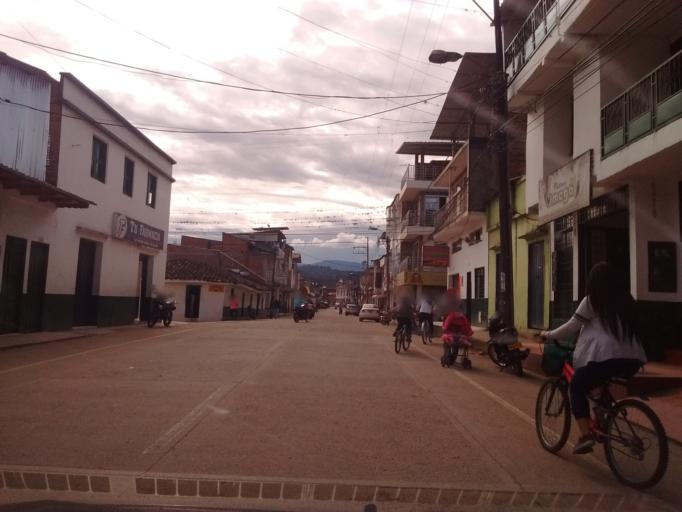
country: CO
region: Huila
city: San Agustin
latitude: 1.8803
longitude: -76.2695
